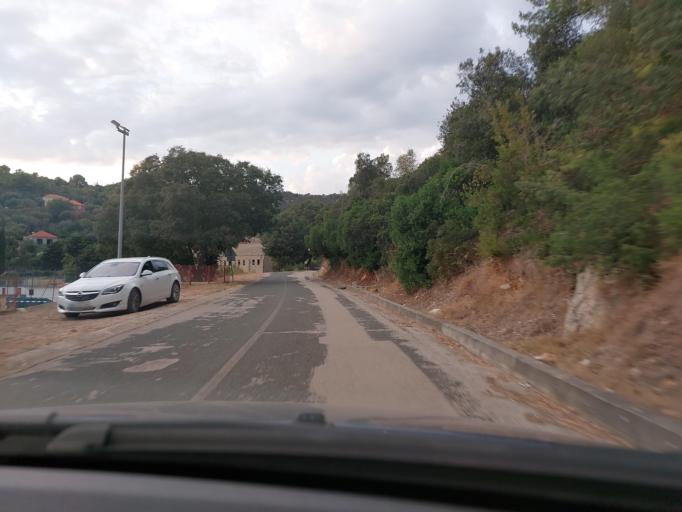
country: HR
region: Dubrovacko-Neretvanska
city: Smokvica
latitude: 42.7644
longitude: 16.8957
